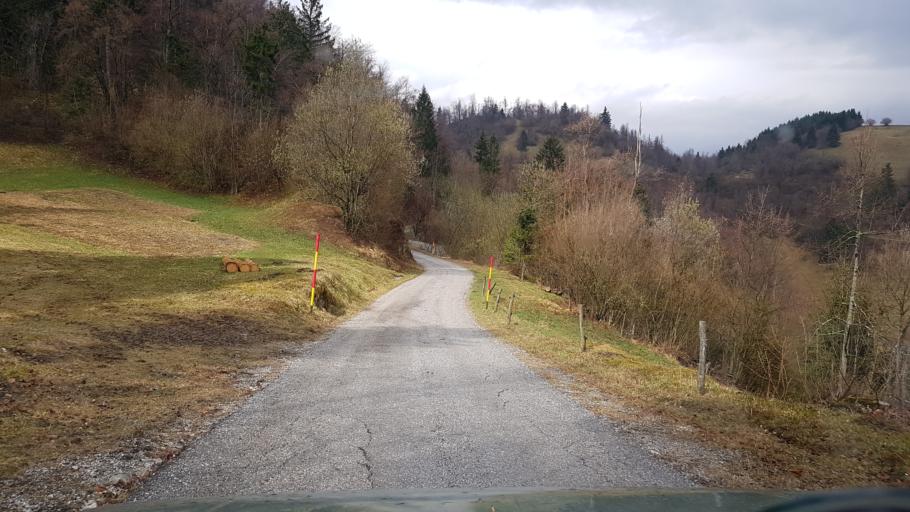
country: SI
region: Cerkno
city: Cerkno
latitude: 46.1397
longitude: 13.8800
